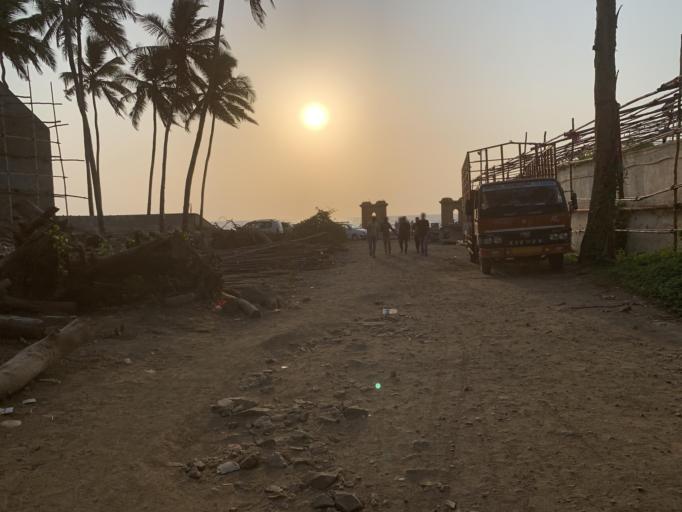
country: IN
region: Daman and Diu
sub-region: Daman District
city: Daman
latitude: 20.4473
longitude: 72.8342
